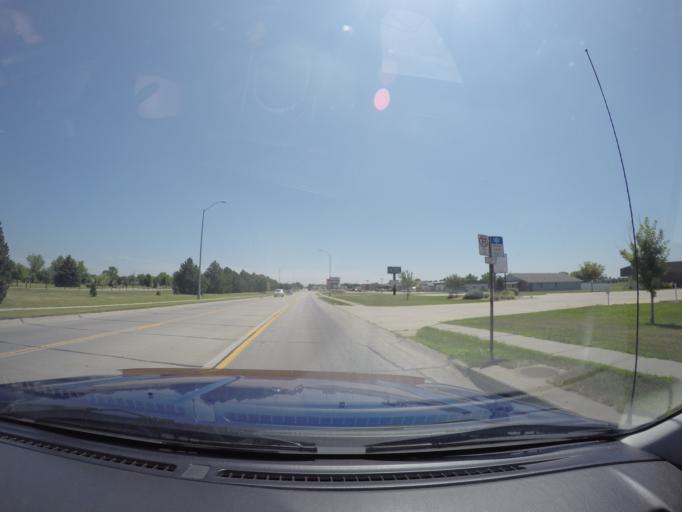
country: US
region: Nebraska
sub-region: Phelps County
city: Holdrege
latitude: 40.4519
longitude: -99.3792
